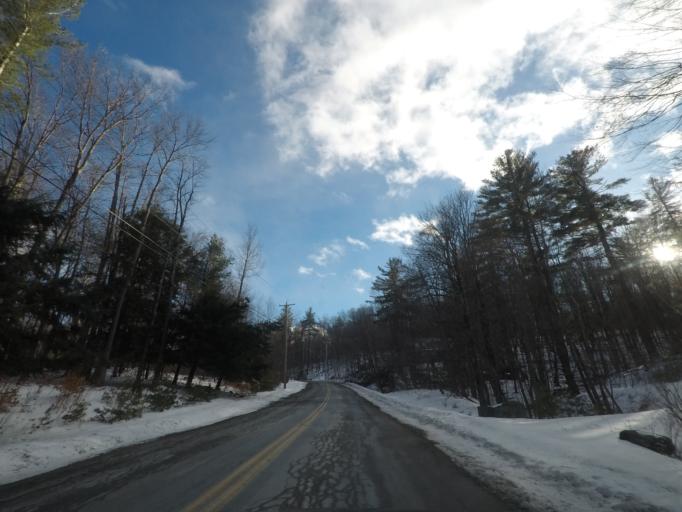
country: US
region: New York
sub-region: Rensselaer County
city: Hoosick Falls
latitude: 42.8170
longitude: -73.3915
